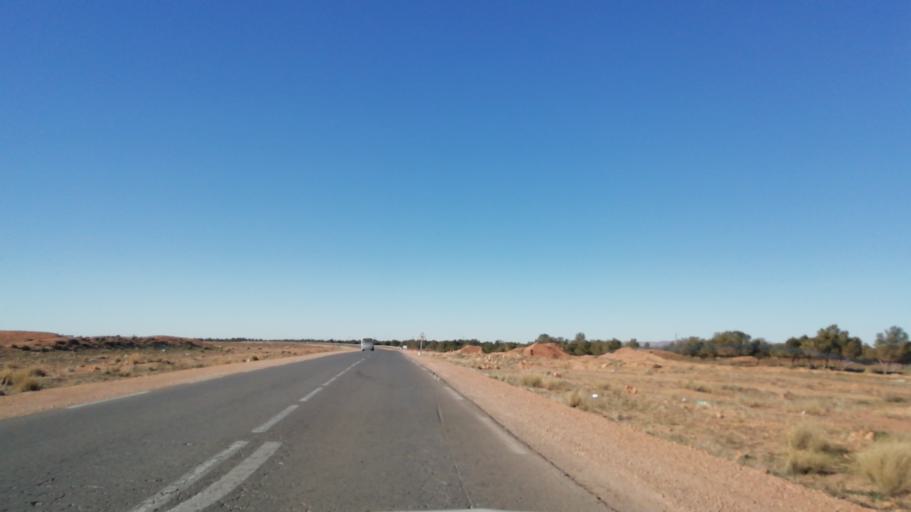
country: DZ
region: El Bayadh
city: El Bayadh
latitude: 33.6658
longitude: 0.9220
